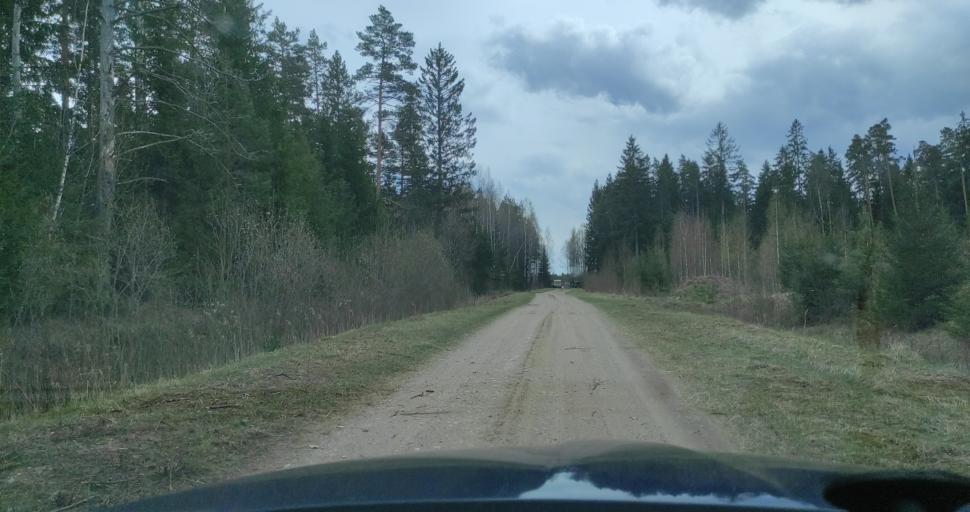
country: LV
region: Dundaga
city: Dundaga
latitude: 57.3587
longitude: 22.1524
